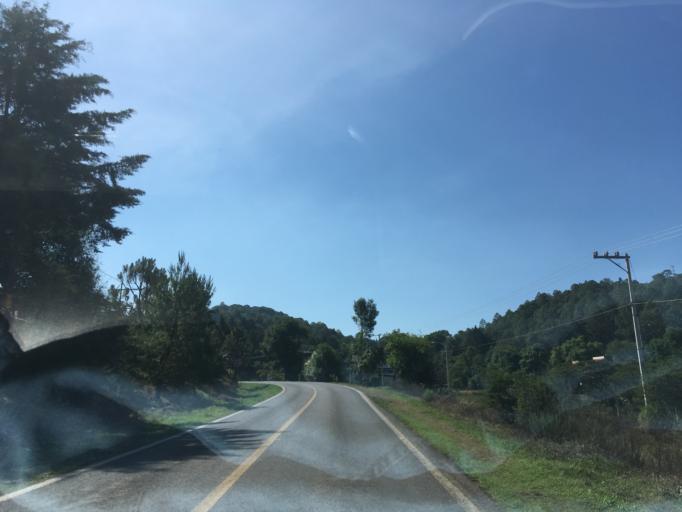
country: MX
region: Michoacan
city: Charo
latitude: 19.6586
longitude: -100.9985
